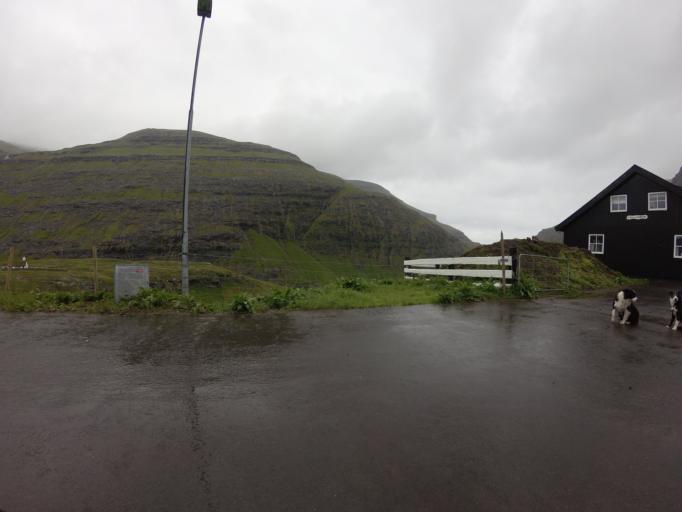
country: FO
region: Streymoy
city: Vestmanna
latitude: 62.2487
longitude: -7.1801
